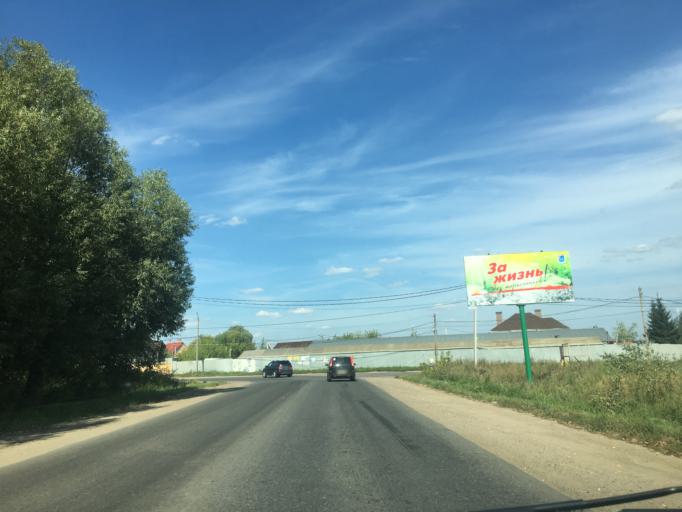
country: RU
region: Moskovskaya
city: Vidnoye
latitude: 55.5098
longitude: 37.6866
